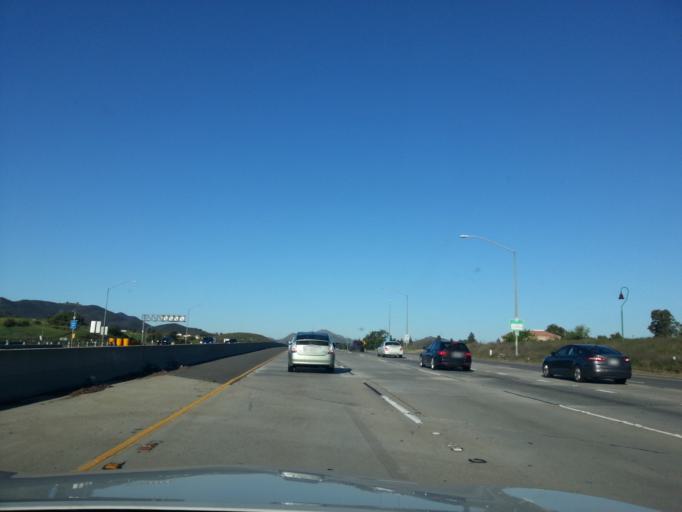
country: US
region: California
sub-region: Ventura County
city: Thousand Oaks
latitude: 34.1763
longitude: -118.8614
